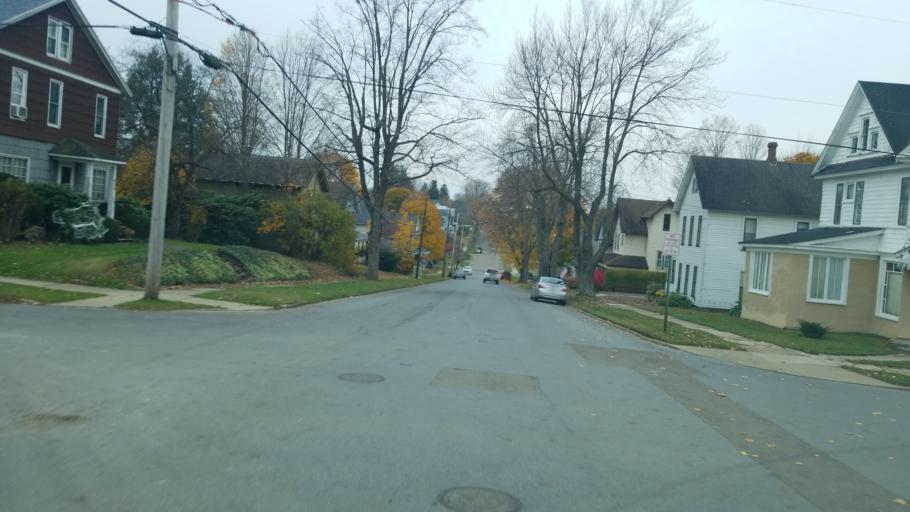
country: US
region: Pennsylvania
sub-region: McKean County
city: Kane
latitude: 41.6619
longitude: -78.8012
